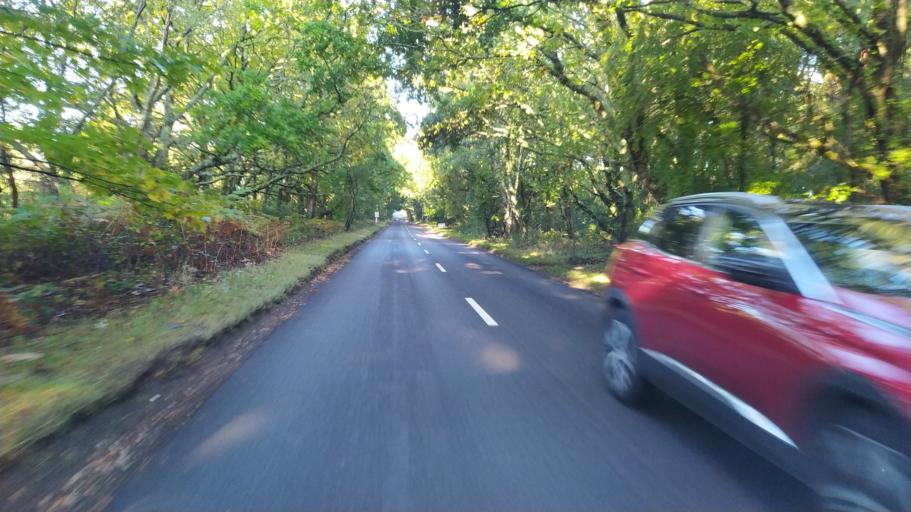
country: GB
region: England
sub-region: Dorset
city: Three Legged Cross
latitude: 50.8530
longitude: -1.8974
